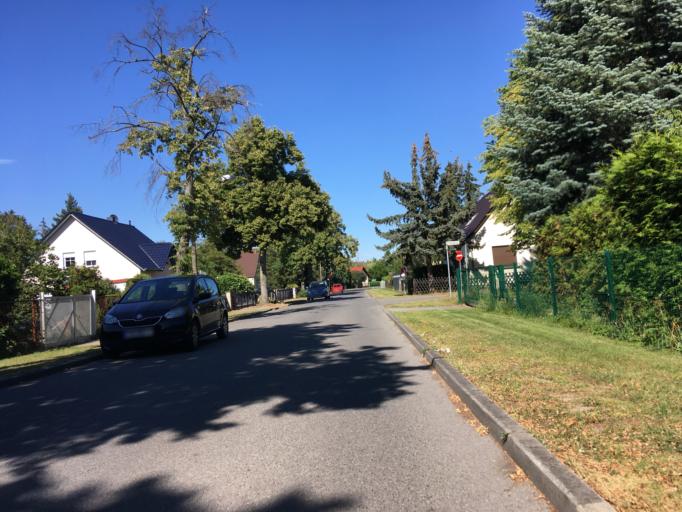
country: DE
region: Brandenburg
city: Schulzendorf
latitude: 52.3613
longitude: 13.5894
